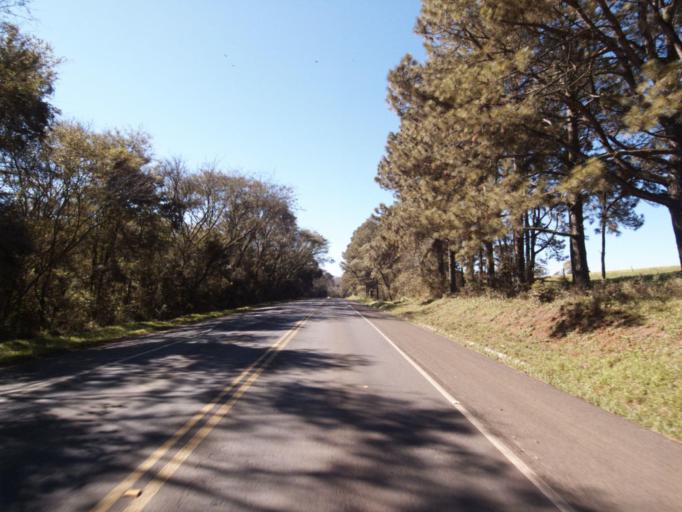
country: BR
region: Santa Catarina
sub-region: Sao Lourenco Do Oeste
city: Sao Lourenco dOeste
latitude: -26.8291
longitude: -53.1191
